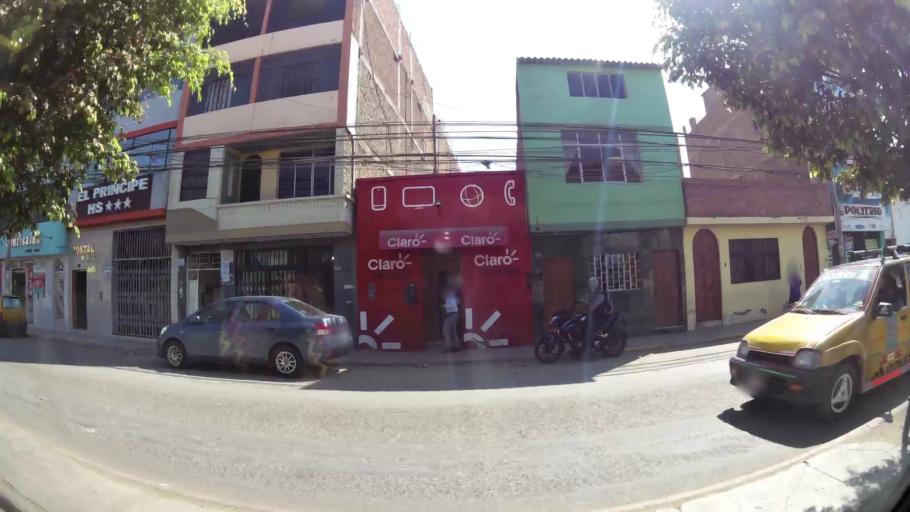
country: PE
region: Lambayeque
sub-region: Provincia de Chiclayo
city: Chiclayo
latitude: -6.7740
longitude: -79.8360
